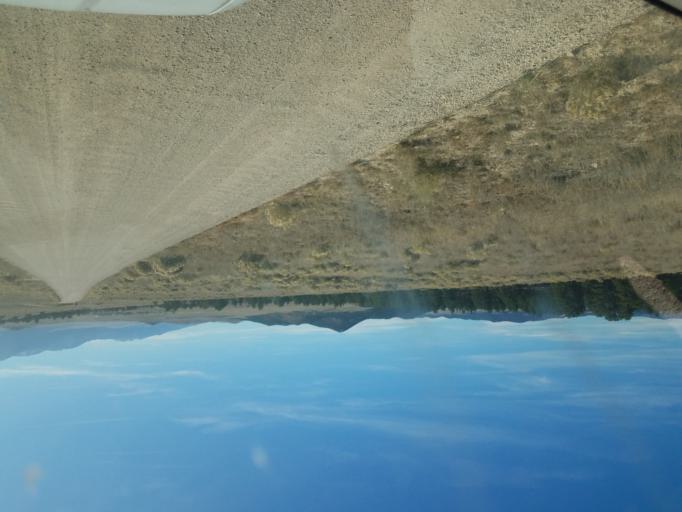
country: US
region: Colorado
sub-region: Custer County
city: Westcliffe
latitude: 38.2297
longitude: -105.4572
